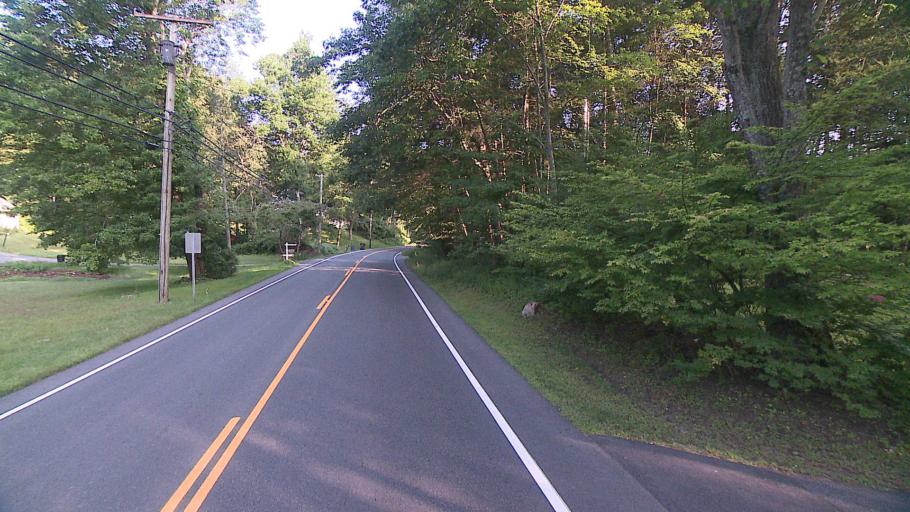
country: US
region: Connecticut
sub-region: Fairfield County
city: Sherman
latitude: 41.6350
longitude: -73.4758
